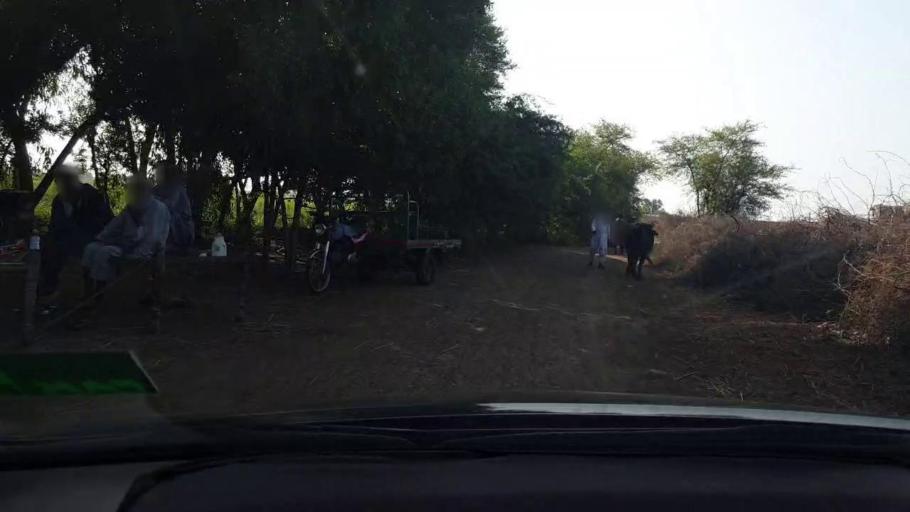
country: PK
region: Sindh
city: Tando Bago
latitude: 24.8013
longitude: 69.0179
